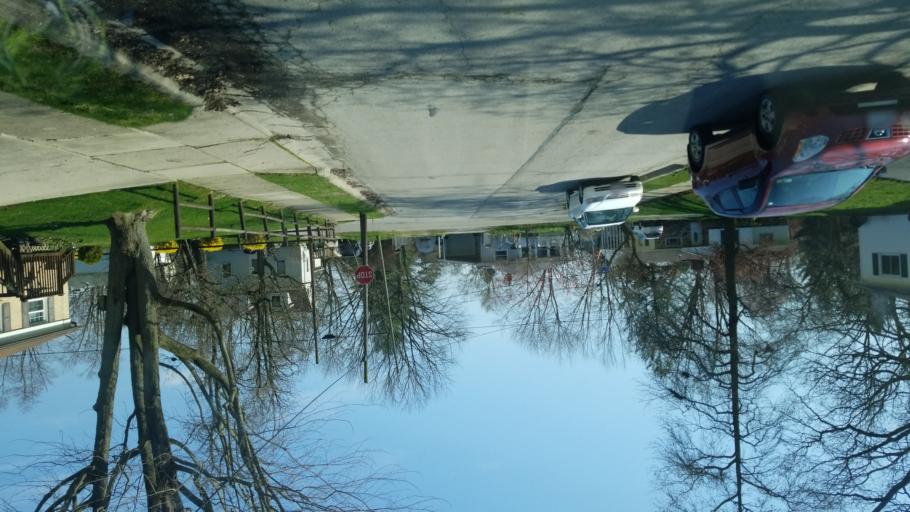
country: US
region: Ohio
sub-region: Delaware County
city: Delaware
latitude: 40.3013
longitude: -83.0523
